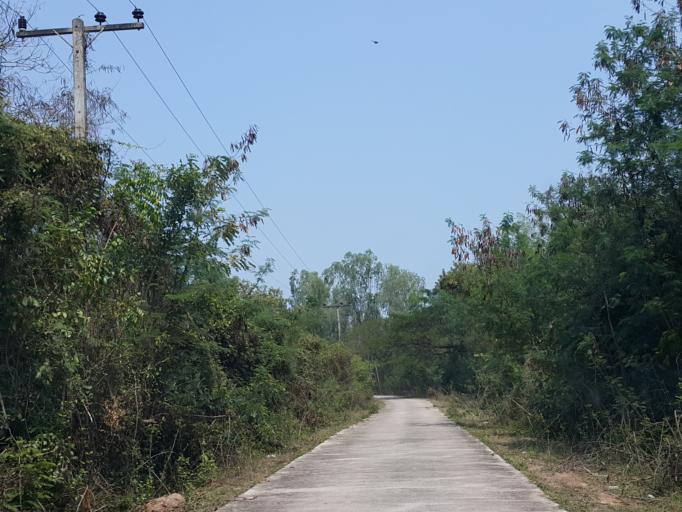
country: TH
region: Lampang
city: Hang Chat
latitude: 18.3005
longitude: 99.4138
